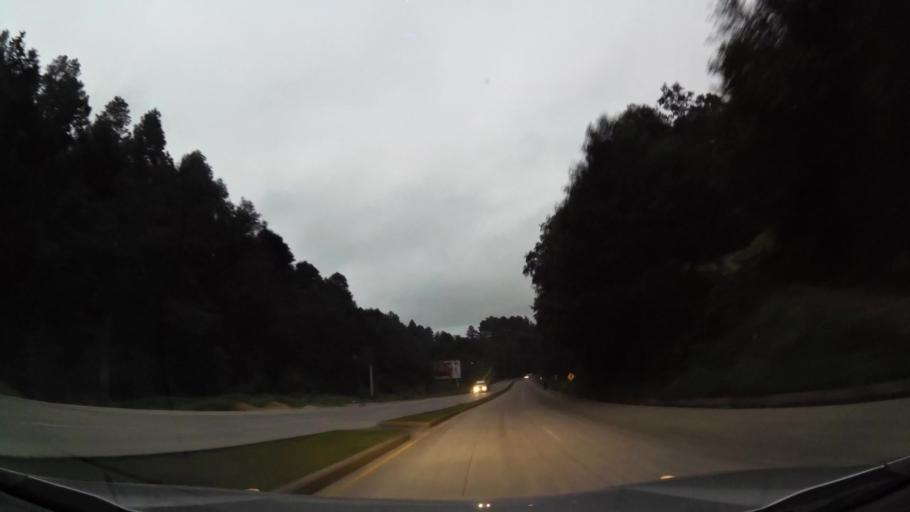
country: GT
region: Chimaltenango
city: Tecpan Guatemala
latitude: 14.8271
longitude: -91.0366
